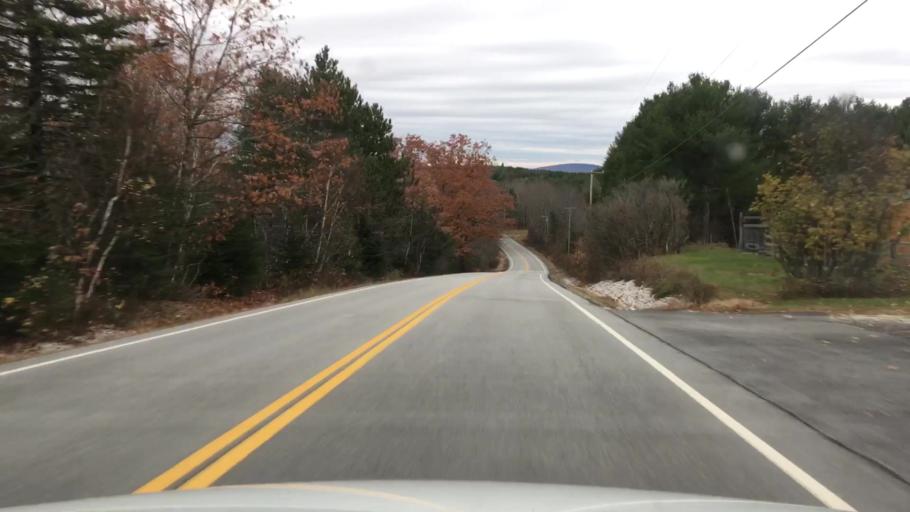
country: US
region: Maine
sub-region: Hancock County
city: Orland
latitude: 44.5366
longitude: -68.6794
